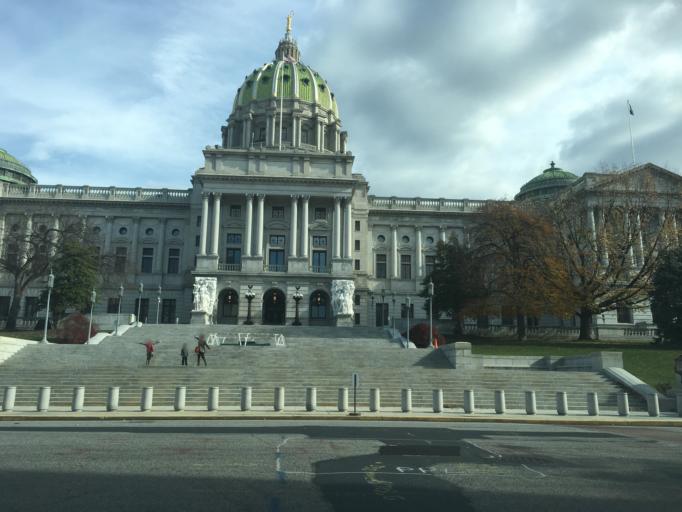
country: US
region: Pennsylvania
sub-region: Dauphin County
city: Harrisburg
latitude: 40.2638
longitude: -76.8850
